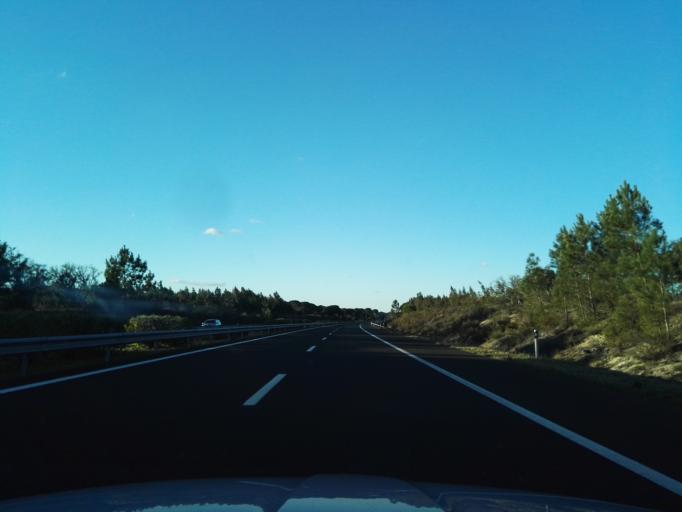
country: PT
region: Santarem
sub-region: Benavente
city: Poceirao
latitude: 38.7349
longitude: -8.6775
